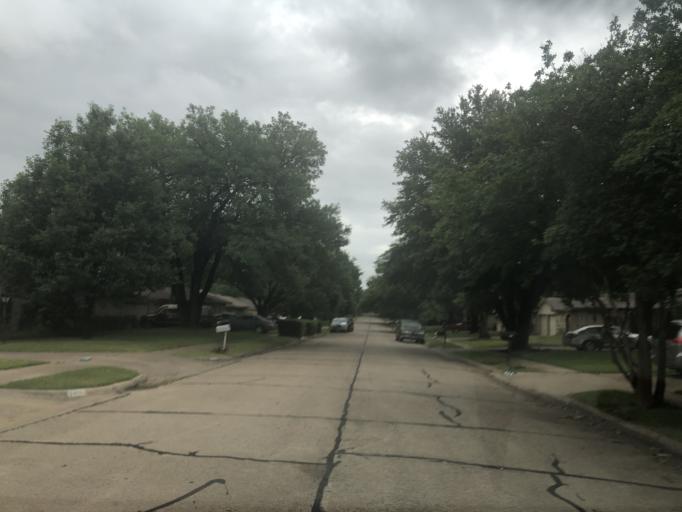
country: US
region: Texas
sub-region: Dallas County
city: Irving
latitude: 32.7963
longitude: -96.9431
